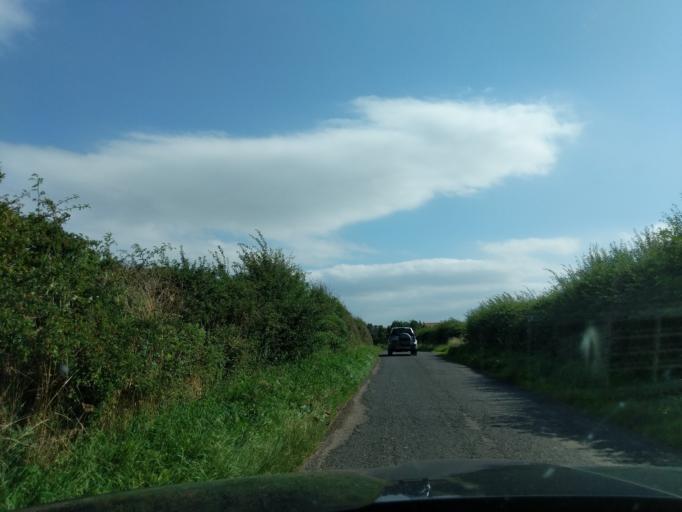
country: GB
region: England
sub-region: Northumberland
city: Ford
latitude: 55.6618
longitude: -2.1574
